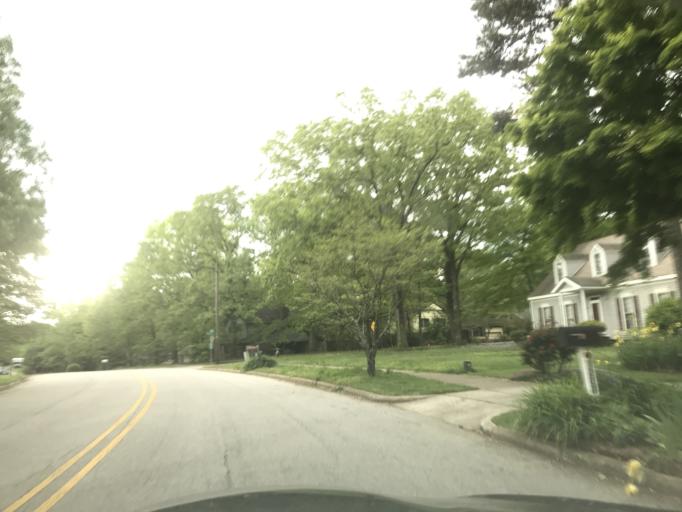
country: US
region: North Carolina
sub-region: Wake County
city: West Raleigh
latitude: 35.7811
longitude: -78.7083
